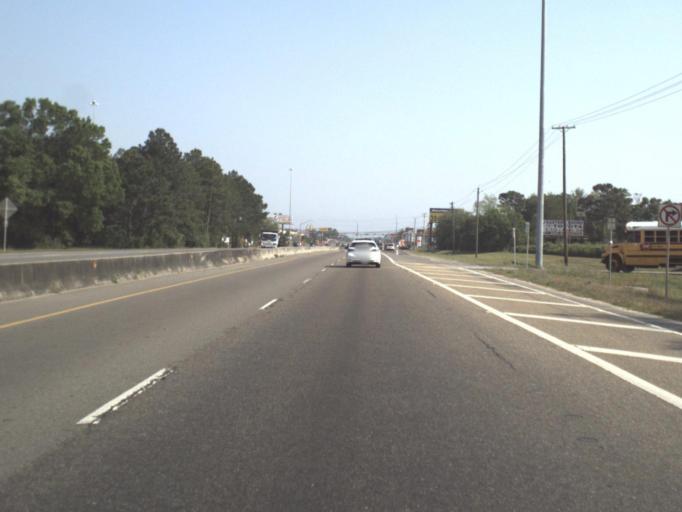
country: US
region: Florida
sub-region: Escambia County
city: Ensley
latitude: 30.5018
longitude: -87.2658
